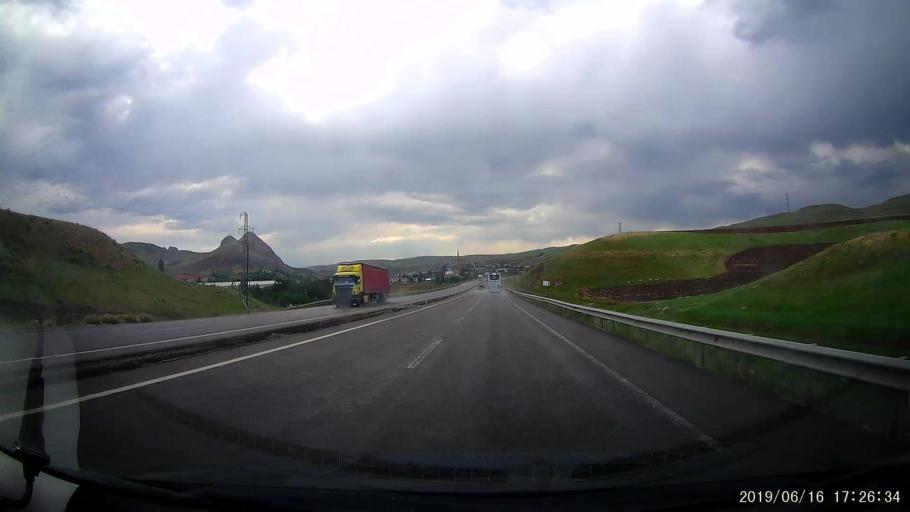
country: TR
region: Erzincan
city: Tercan
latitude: 39.7688
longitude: 40.4097
